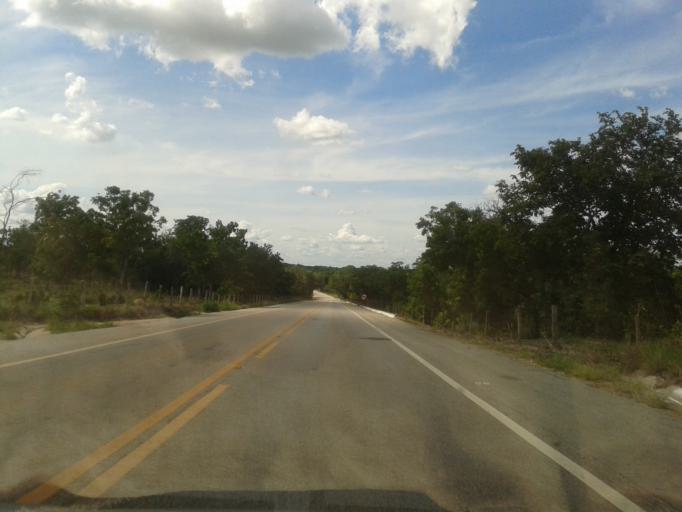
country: BR
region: Goias
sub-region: Itapuranga
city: Itapuranga
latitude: -15.4888
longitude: -50.3236
